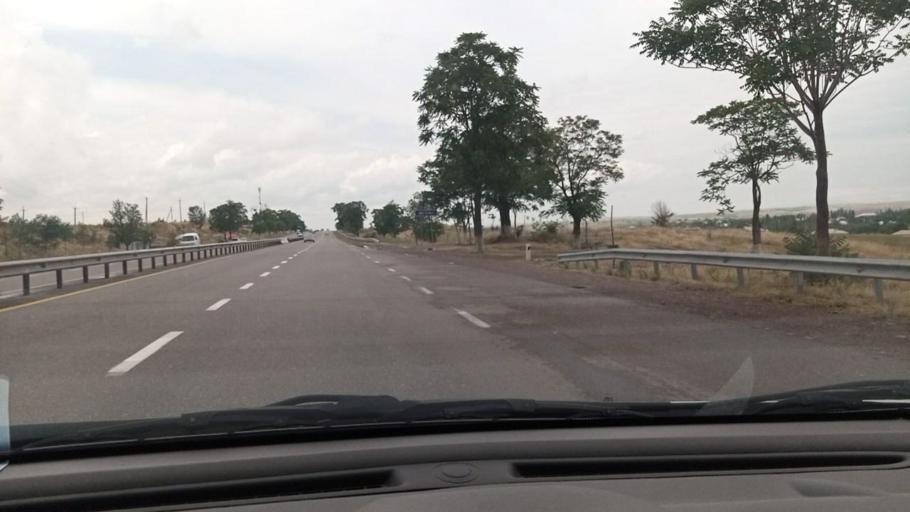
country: UZ
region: Toshkent
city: Ohangaron
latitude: 40.9779
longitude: 69.5425
